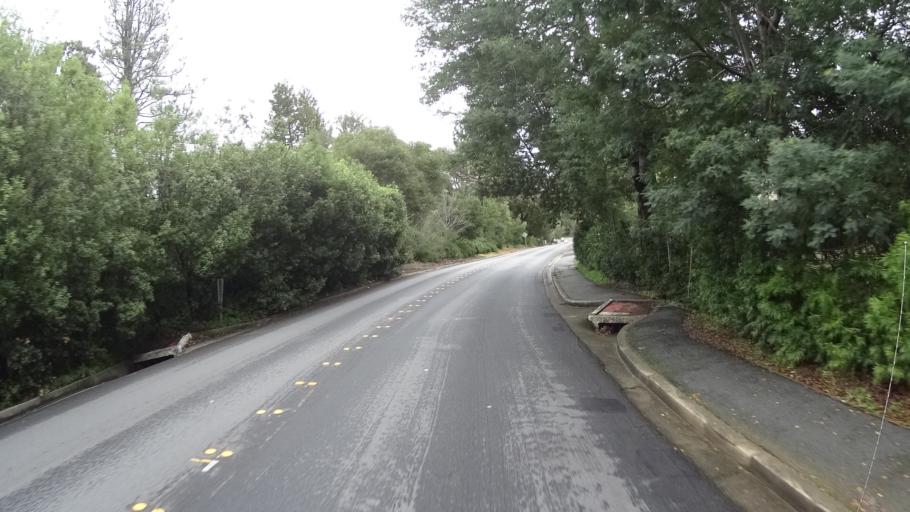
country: US
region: California
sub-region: San Mateo County
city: Hillsborough
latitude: 37.5641
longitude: -122.3658
